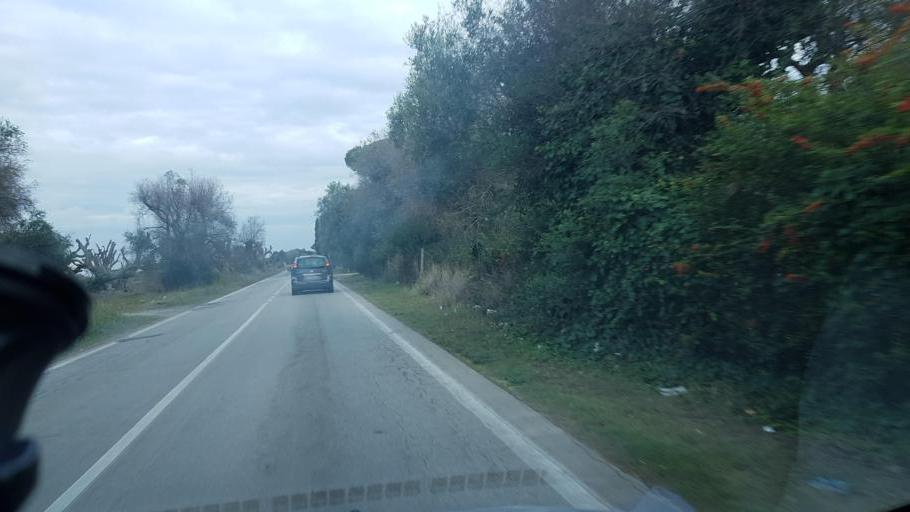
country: IT
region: Apulia
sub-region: Provincia di Brindisi
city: Oria
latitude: 40.5148
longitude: 17.6149
